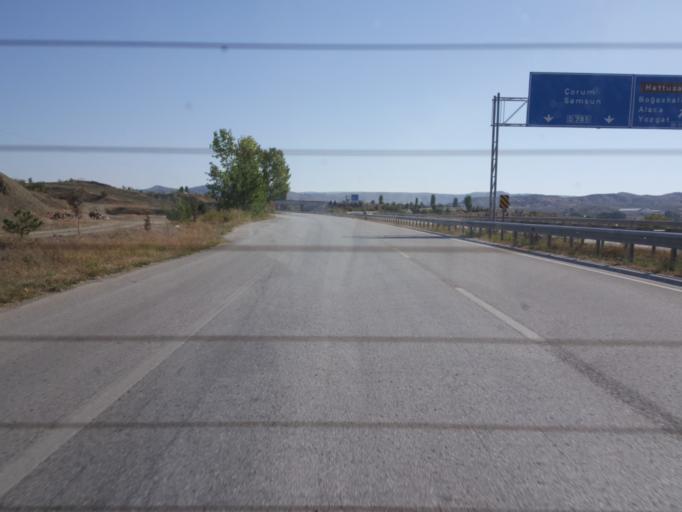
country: TR
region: Corum
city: Sungurlu
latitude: 40.1771
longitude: 34.4592
